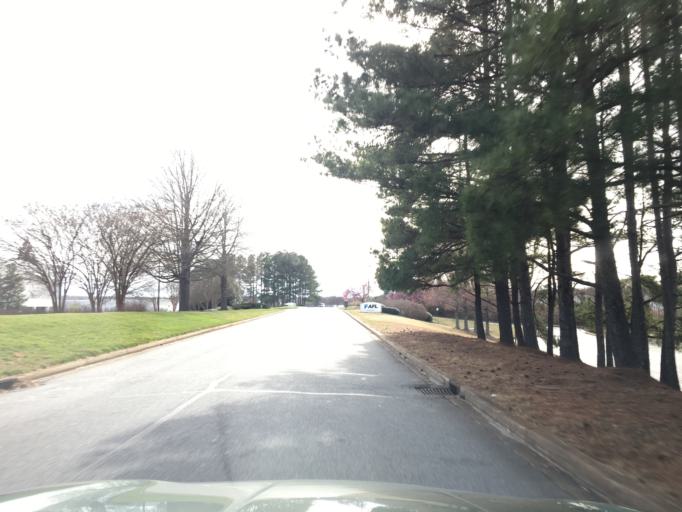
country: US
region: South Carolina
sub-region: Spartanburg County
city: Wellford
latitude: 34.9009
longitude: -82.1059
